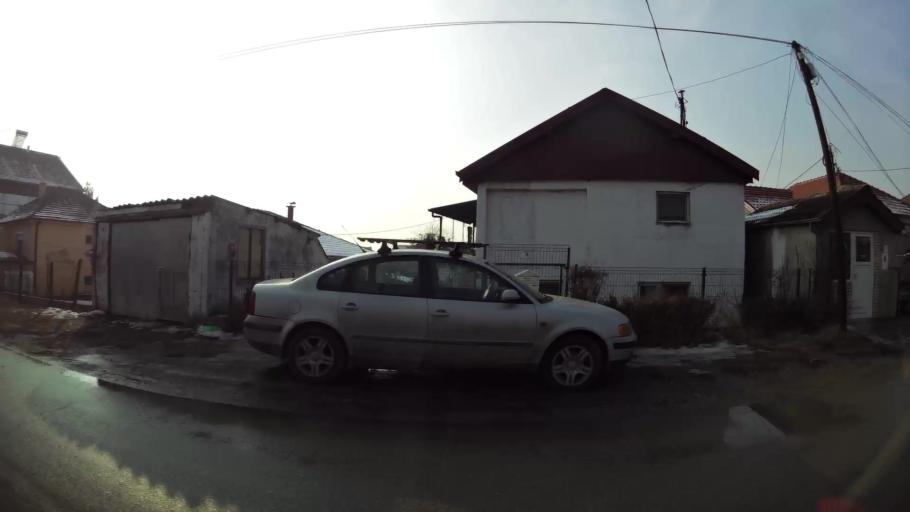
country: MK
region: Ilinden
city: Marino
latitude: 41.9846
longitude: 21.5947
